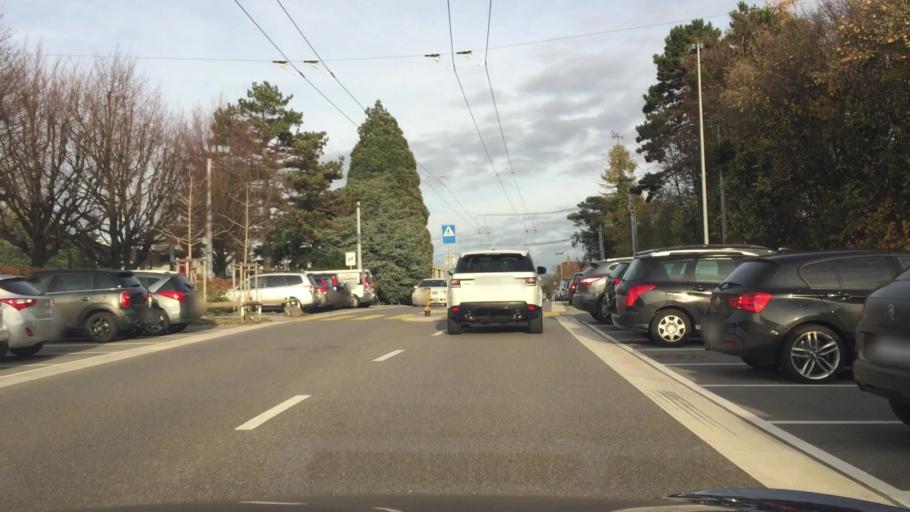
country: CH
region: Vaud
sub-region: Ouest Lausannois District
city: Renens
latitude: 46.5295
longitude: 6.5844
